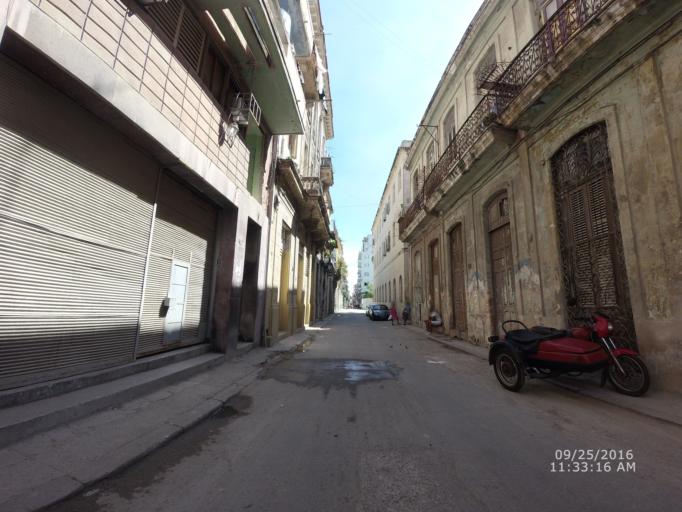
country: CU
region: La Habana
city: La Habana Vieja
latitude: 23.1363
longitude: -82.3567
